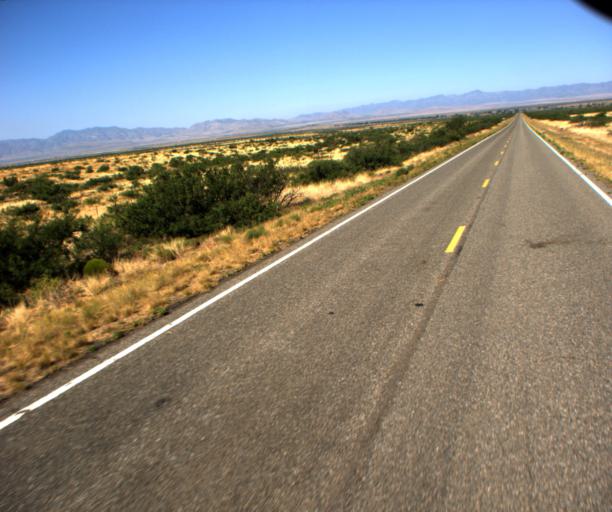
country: US
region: Arizona
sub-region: Graham County
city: Swift Trail Junction
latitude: 32.5870
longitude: -109.9209
